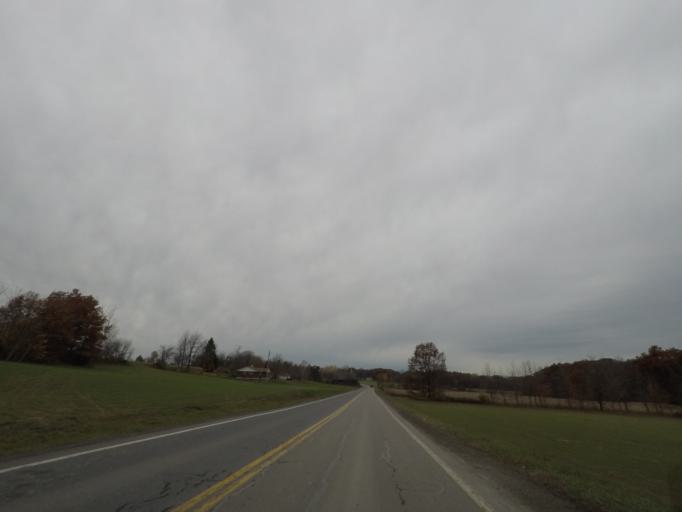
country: US
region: New York
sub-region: Saratoga County
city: Mechanicville
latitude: 42.8533
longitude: -73.7084
